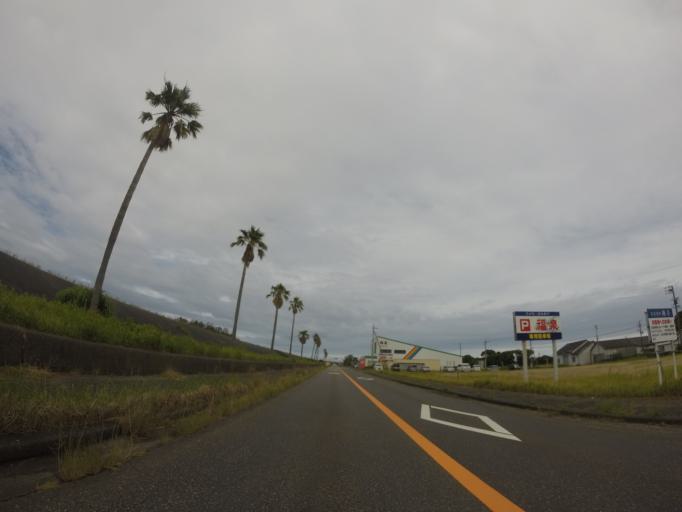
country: JP
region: Shizuoka
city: Oyama
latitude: 34.6036
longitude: 138.2298
